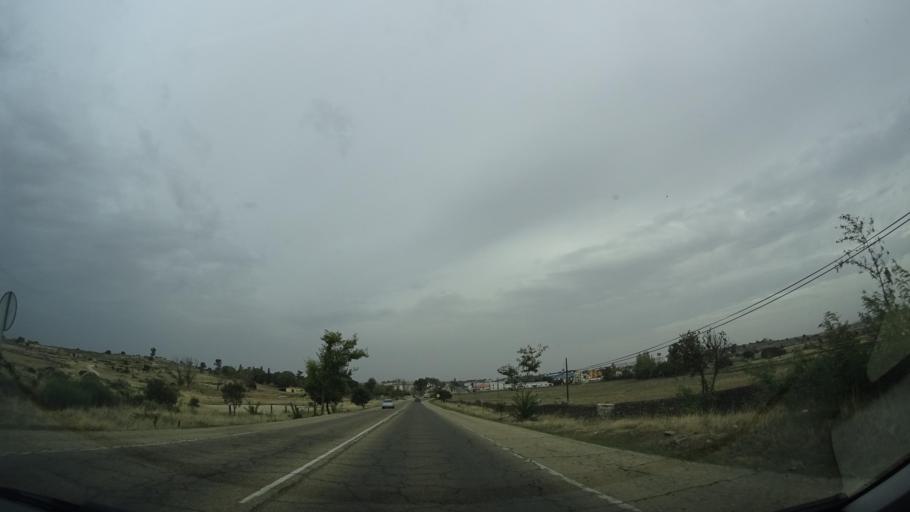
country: ES
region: Extremadura
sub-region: Provincia de Caceres
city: Trujillo
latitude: 39.4708
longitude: -5.8616
